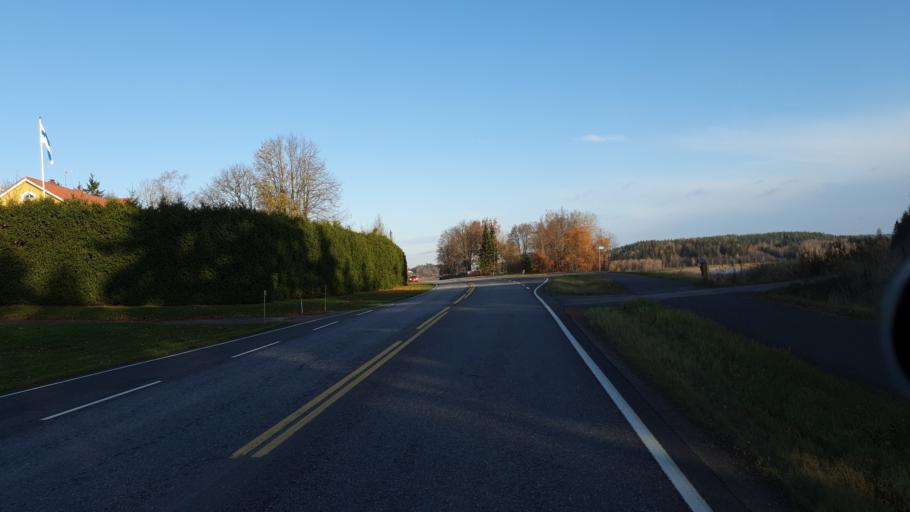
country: FI
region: Uusimaa
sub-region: Helsinki
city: Siuntio
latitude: 60.1539
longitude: 24.2070
